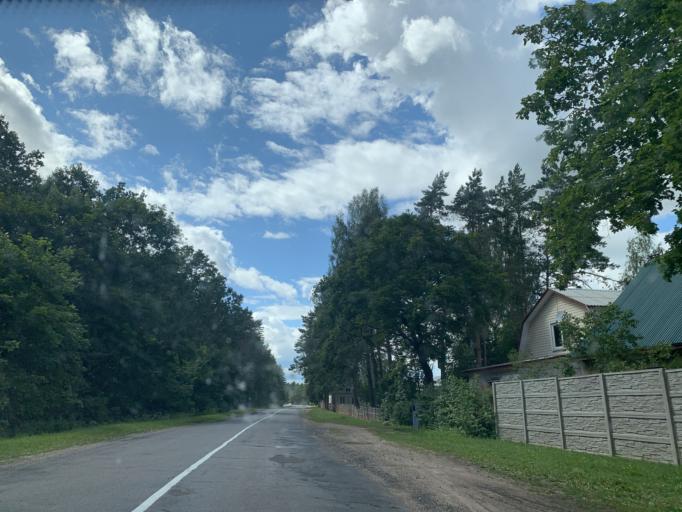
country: BY
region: Minsk
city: Rakaw
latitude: 53.9860
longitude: 26.9516
